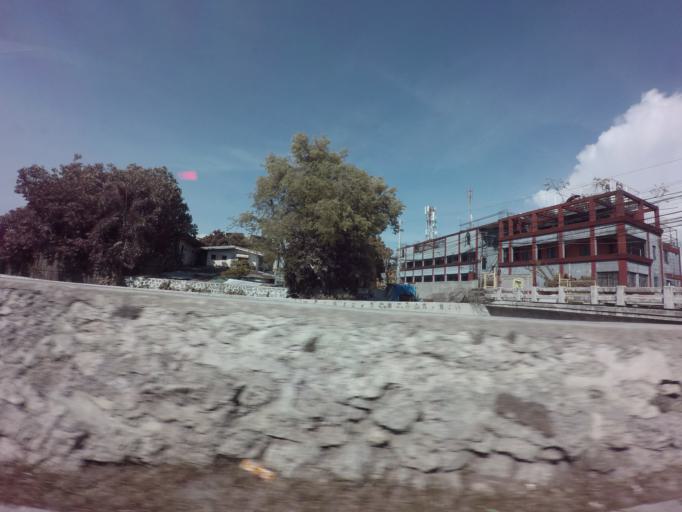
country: PH
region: Calabarzon
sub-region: Province of Rizal
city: Las Pinas
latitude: 14.4666
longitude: 120.9831
